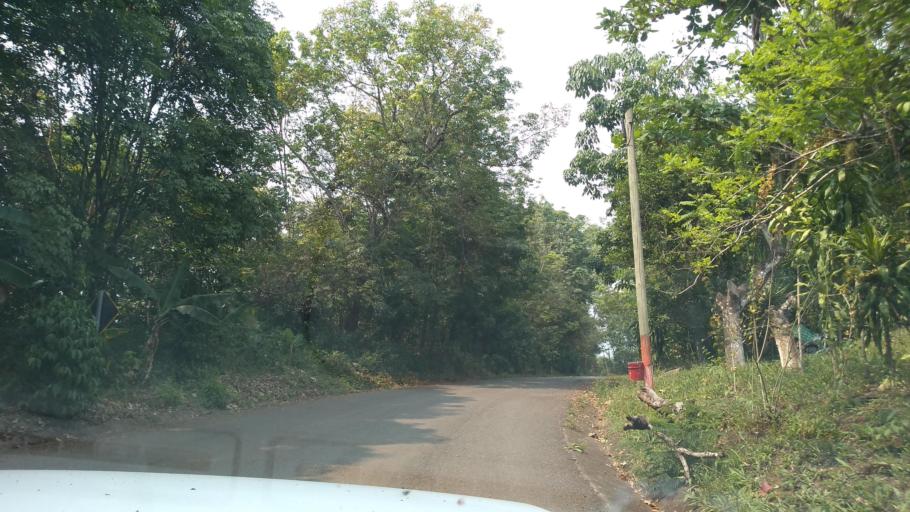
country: MX
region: Veracruz
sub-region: Tezonapa
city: Laguna Chica (Pueblo Nuevo)
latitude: 18.5319
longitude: -96.7882
